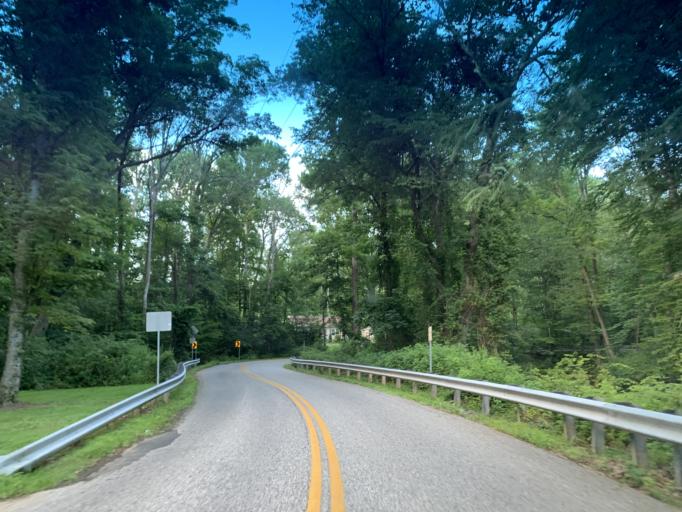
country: US
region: Maryland
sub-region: Harford County
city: Aberdeen
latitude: 39.5352
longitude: -76.1637
